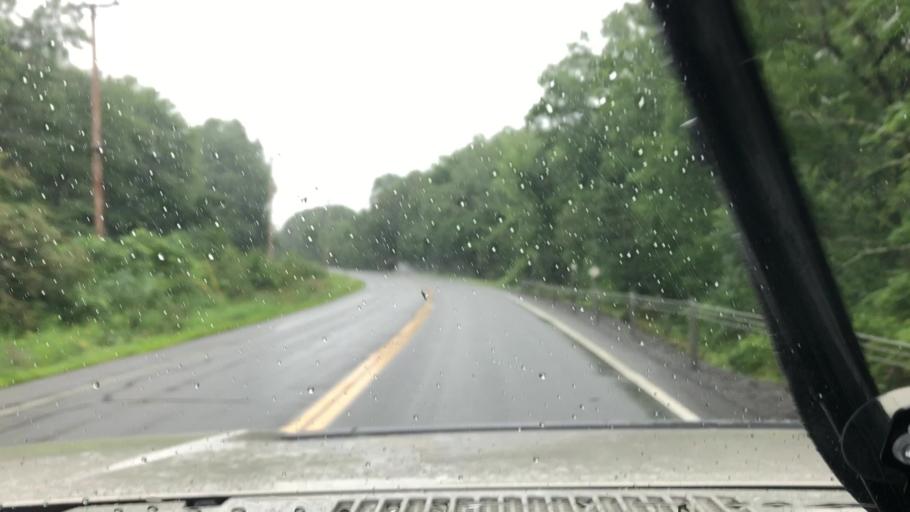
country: US
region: New York
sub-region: Greene County
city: Cairo
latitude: 42.2681
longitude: -73.9747
